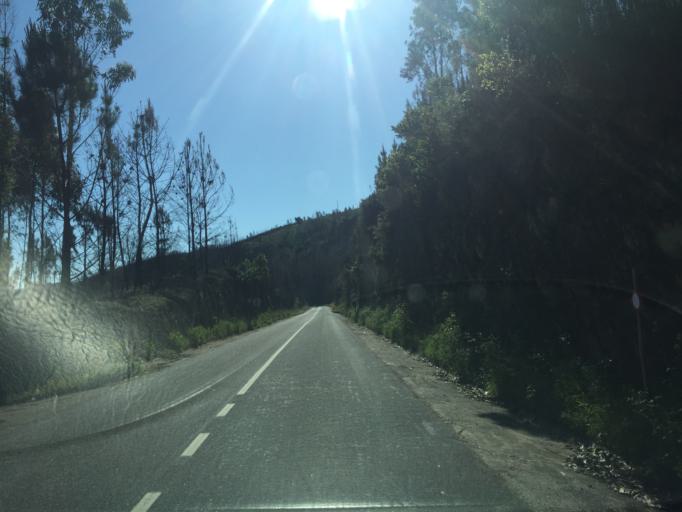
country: PT
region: Coimbra
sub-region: Pampilhosa da Serra
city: Pampilhosa da Serra
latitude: 40.0405
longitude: -7.9132
